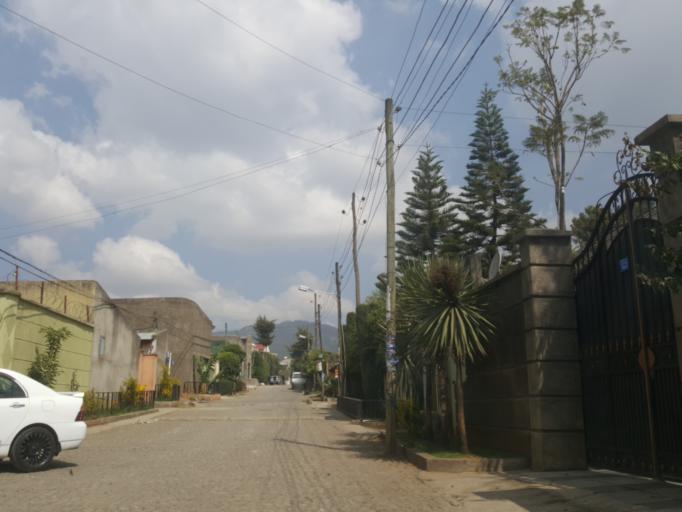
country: ET
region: Adis Abeba
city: Addis Ababa
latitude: 9.0589
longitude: 38.7207
